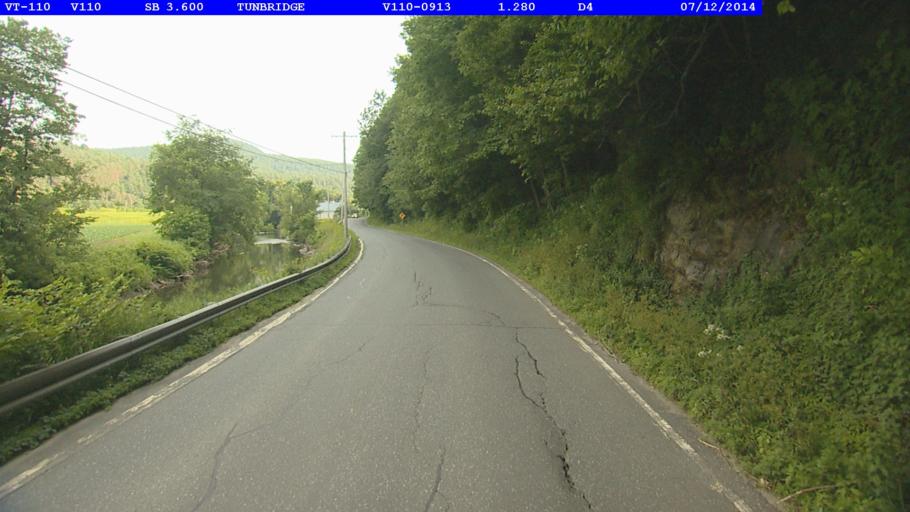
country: US
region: Vermont
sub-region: Orange County
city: Chelsea
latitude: 43.8692
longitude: -72.4993
